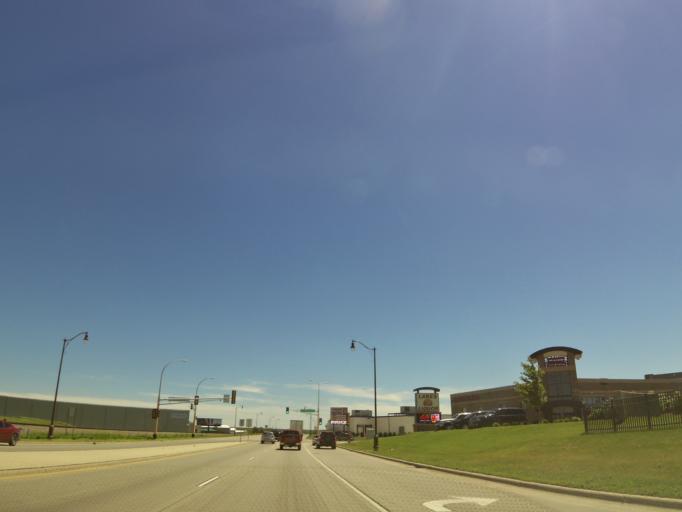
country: US
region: Minnesota
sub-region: Becker County
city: Detroit Lakes
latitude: 46.8182
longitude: -95.8427
